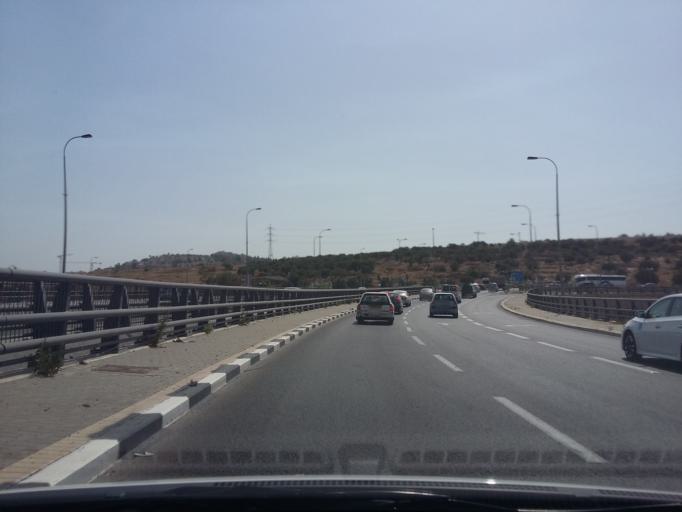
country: PS
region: West Bank
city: Bir Nabala
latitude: 31.8257
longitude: 35.2158
